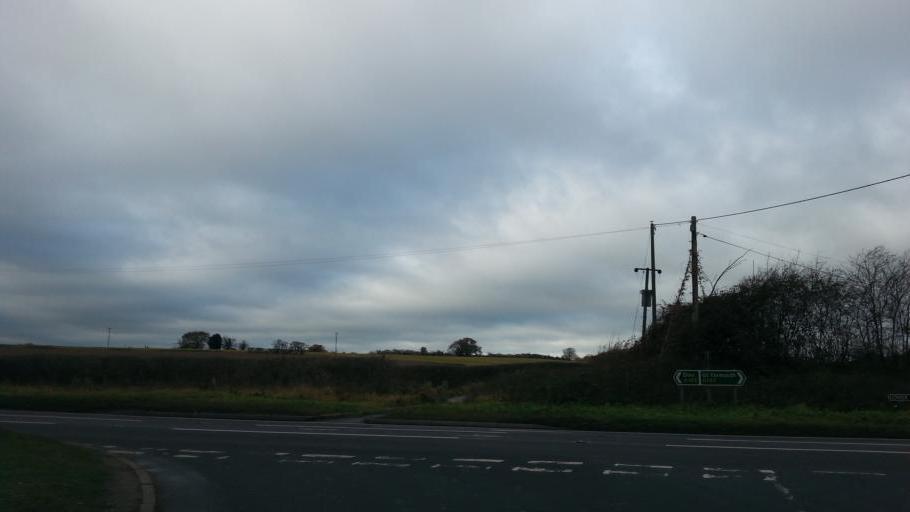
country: GB
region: England
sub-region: Norfolk
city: Diss
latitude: 52.3630
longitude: 1.1800
